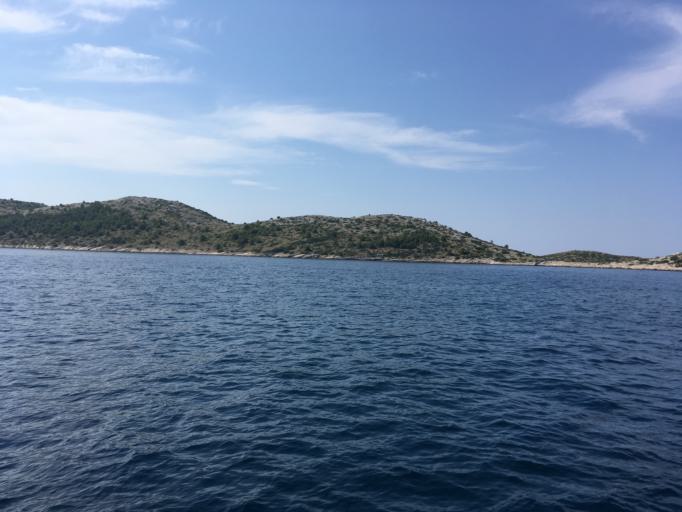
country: HR
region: Zadarska
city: Sali
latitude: 43.8371
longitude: 15.2368
